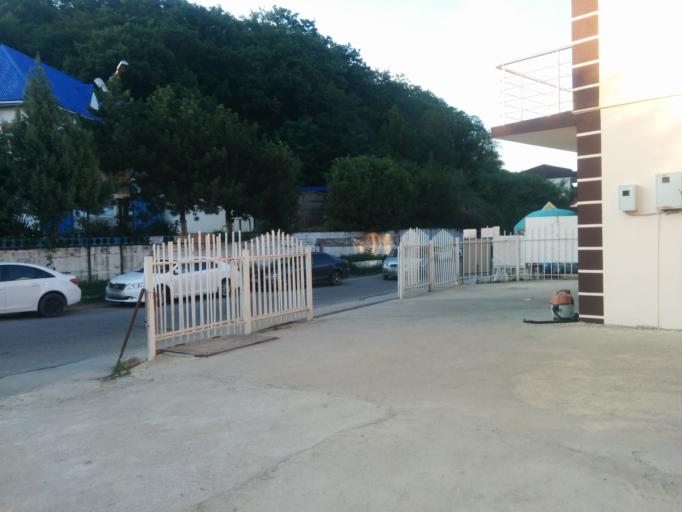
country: RU
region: Krasnodarskiy
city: Novomikhaylovskiy
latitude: 44.2605
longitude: 38.8219
